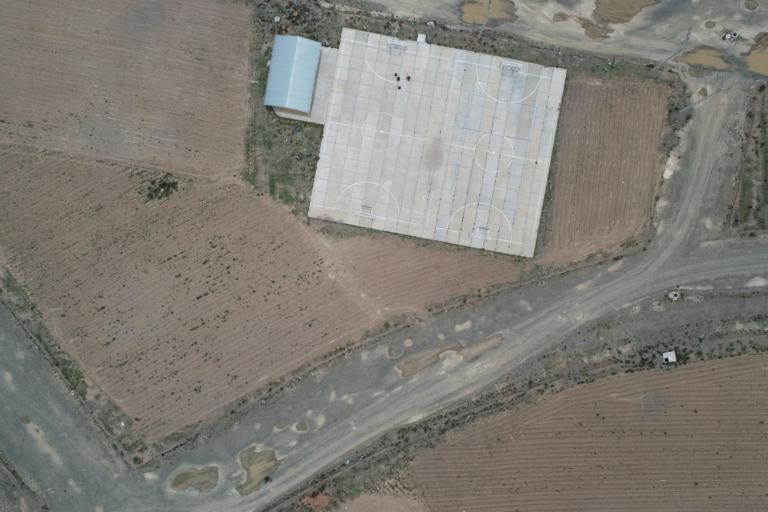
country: BO
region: La Paz
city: La Paz
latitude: -16.5189
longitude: -68.2982
